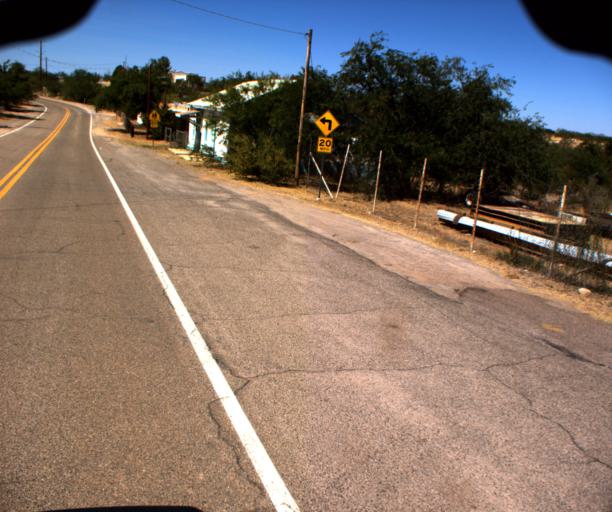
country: US
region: Arizona
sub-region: Santa Cruz County
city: Tubac
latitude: 31.4882
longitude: -111.5427
